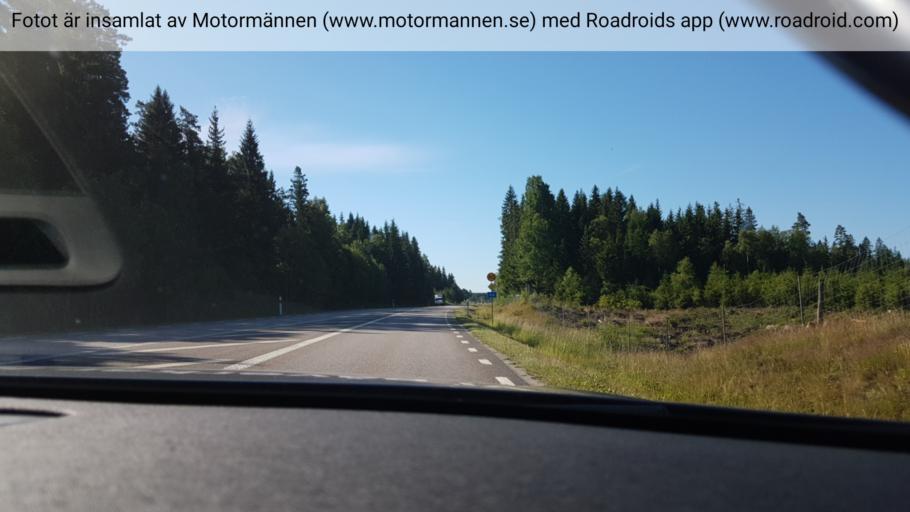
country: SE
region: Vaestra Goetaland
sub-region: Falkopings Kommun
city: Falkoeping
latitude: 58.0576
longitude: 13.5422
